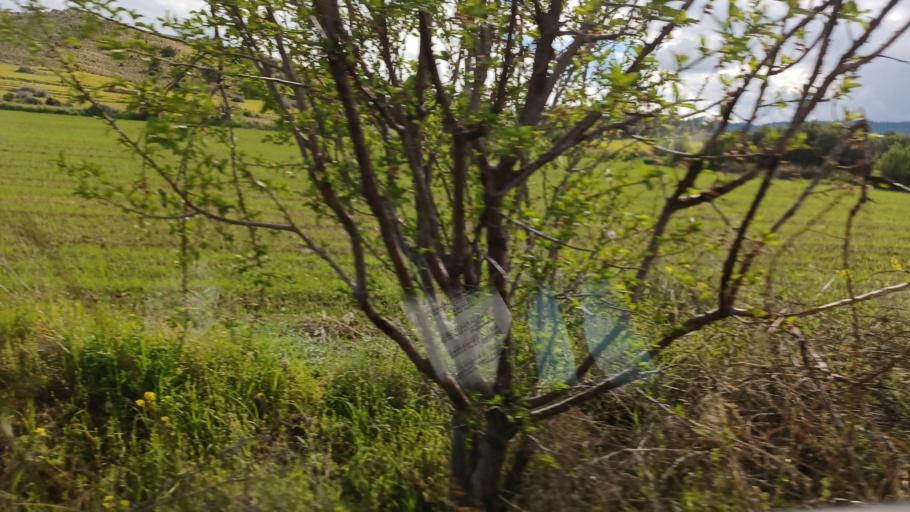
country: CY
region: Lefkosia
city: Lefka
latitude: 35.0750
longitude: 32.9258
